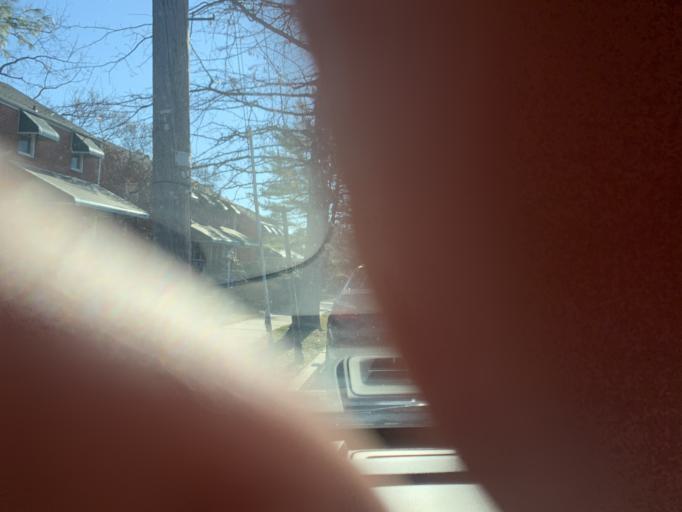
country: US
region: Maryland
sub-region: Baltimore County
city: Lochearn
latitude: 39.3369
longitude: -76.6774
